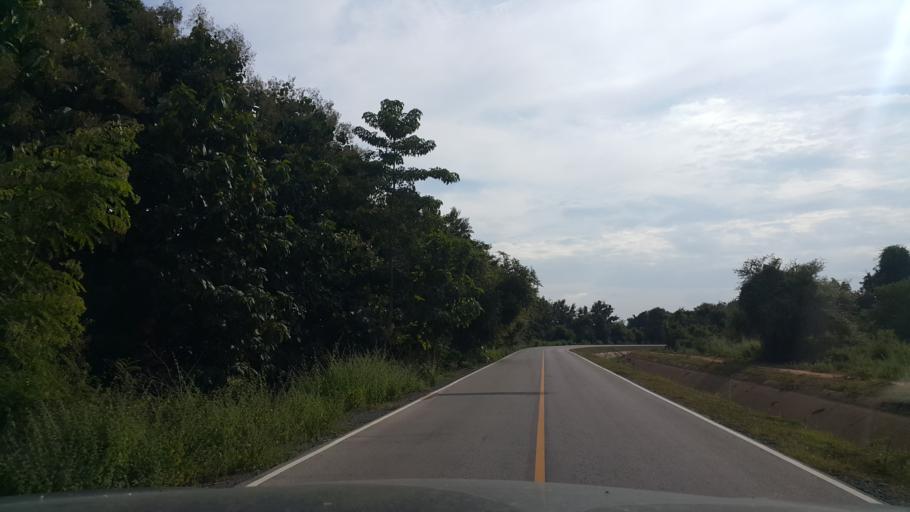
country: TH
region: Chiang Mai
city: San Sai
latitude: 18.9142
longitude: 99.1120
